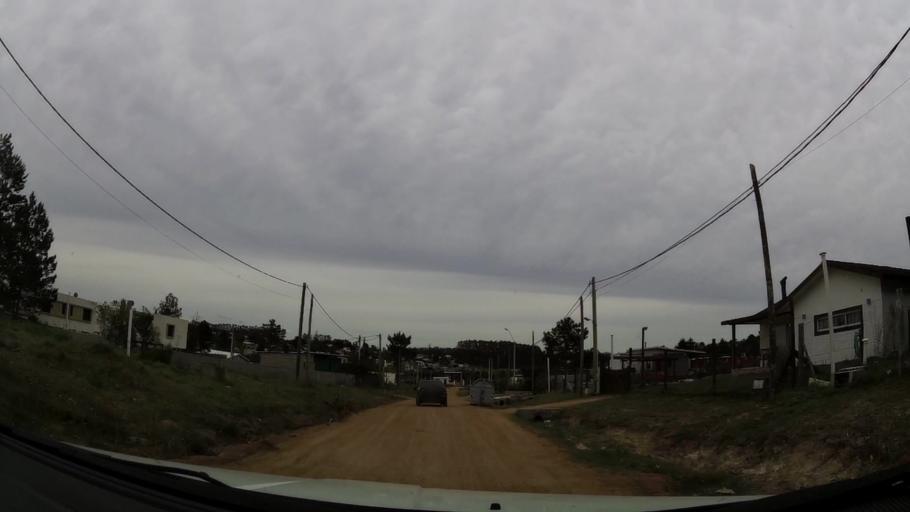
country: UY
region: Maldonado
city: Maldonado
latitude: -34.8971
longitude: -54.9906
